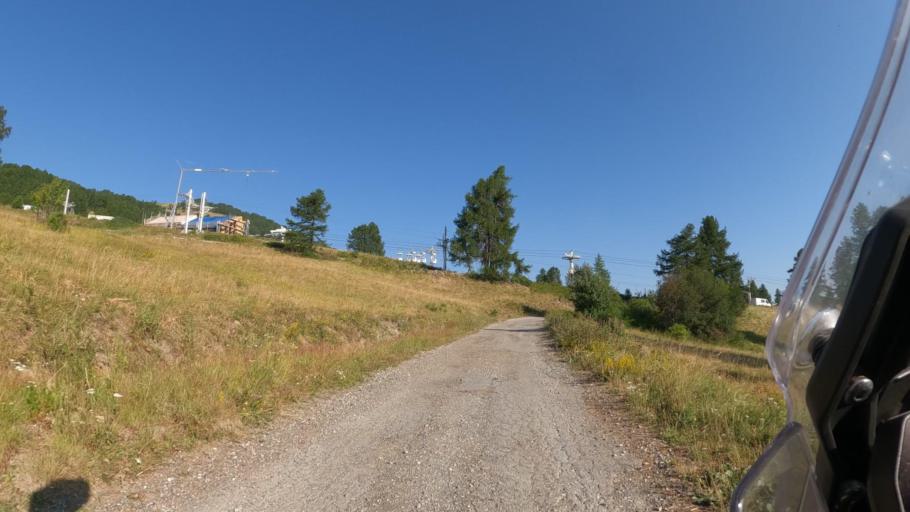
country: FR
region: Provence-Alpes-Cote d'Azur
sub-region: Departement des Hautes-Alpes
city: Guillestre
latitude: 44.6183
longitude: 6.6317
